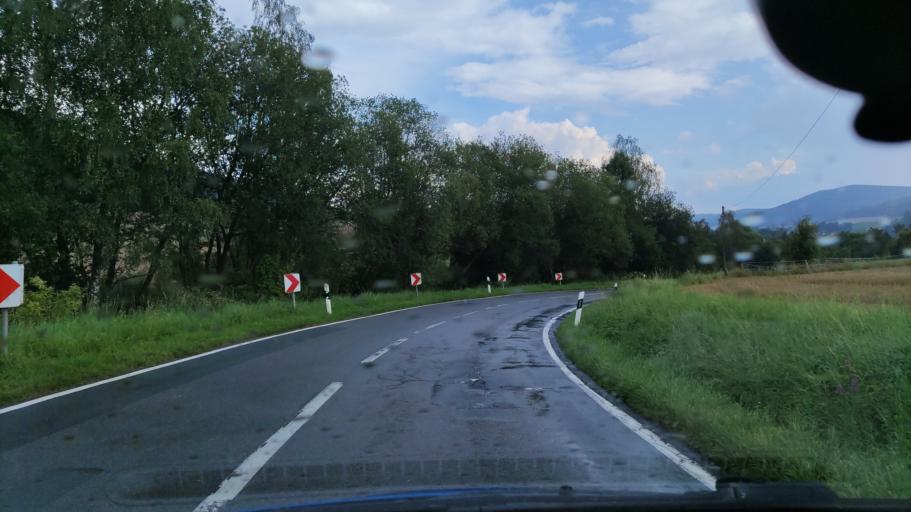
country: DE
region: Lower Saxony
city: Delligsen
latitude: 51.9529
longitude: 9.7922
